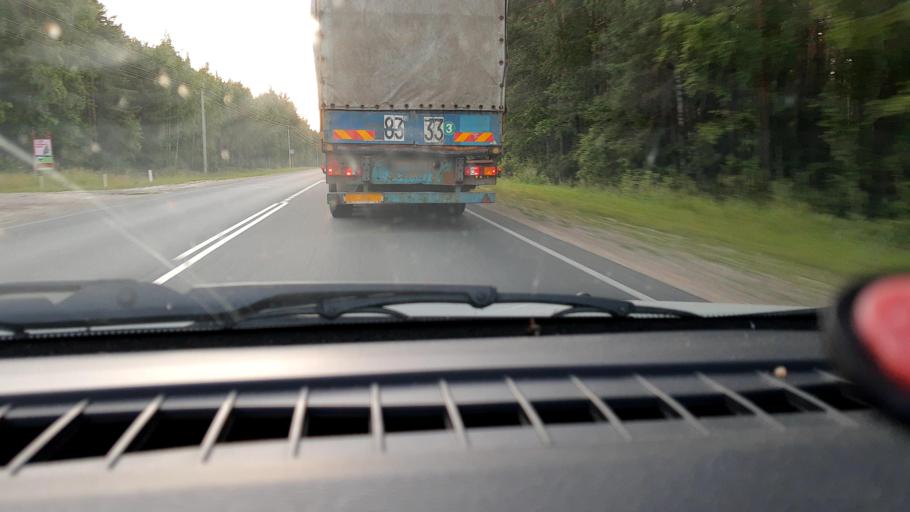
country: RU
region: Nizjnij Novgorod
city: Uren'
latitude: 57.3544
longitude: 45.7025
